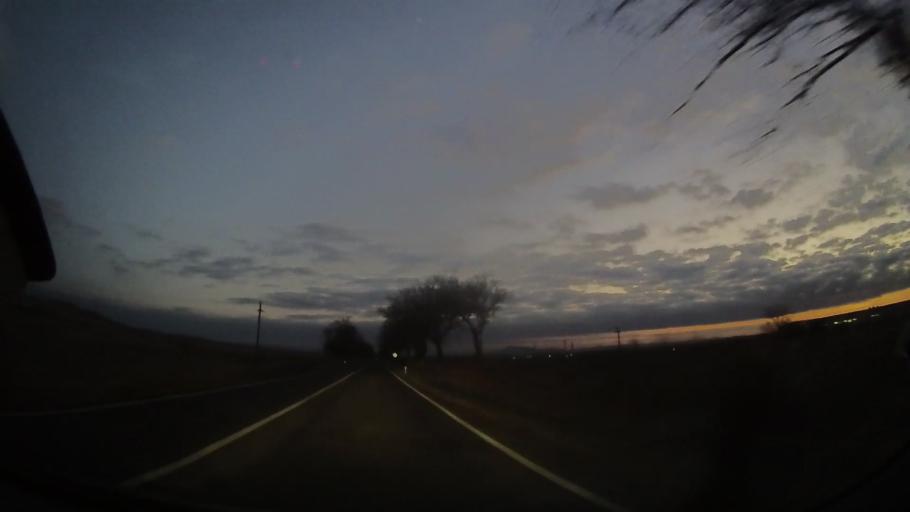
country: RO
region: Tulcea
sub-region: Comuna Frecatei
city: Cataloi
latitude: 45.1039
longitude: 28.7426
